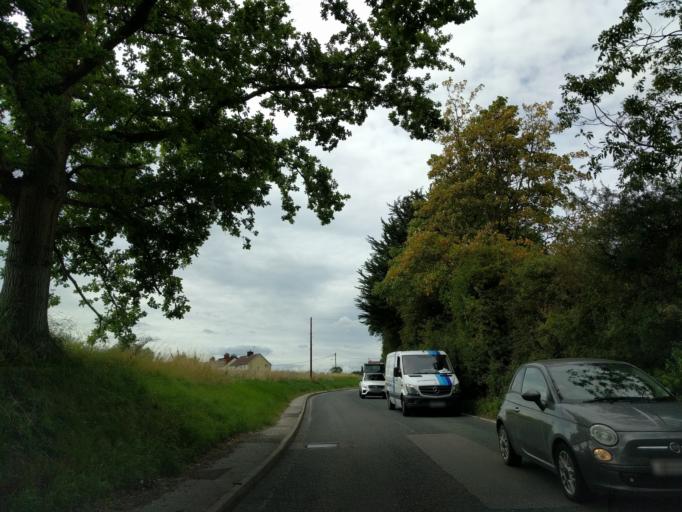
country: GB
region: England
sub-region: Essex
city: Great Dunmow
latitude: 51.8677
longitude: 0.4151
